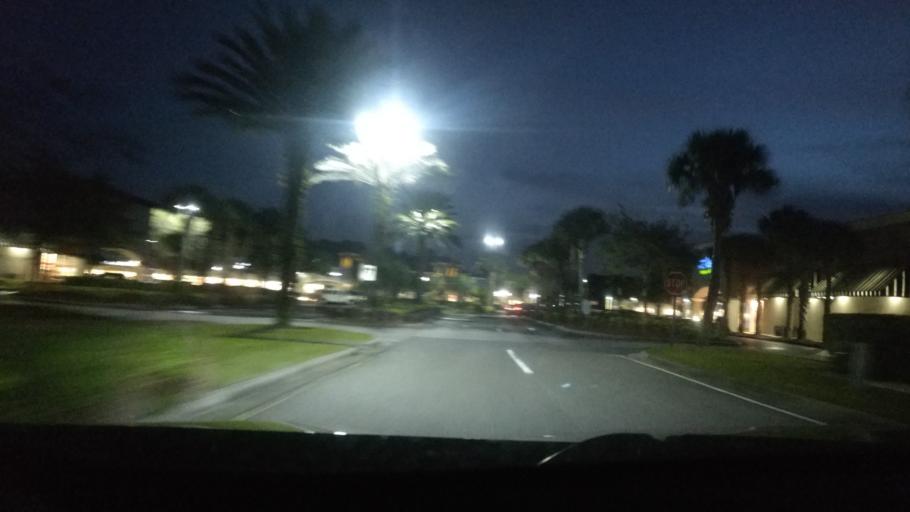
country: US
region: Florida
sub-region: Osceola County
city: Celebration
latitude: 28.3509
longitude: -81.4880
